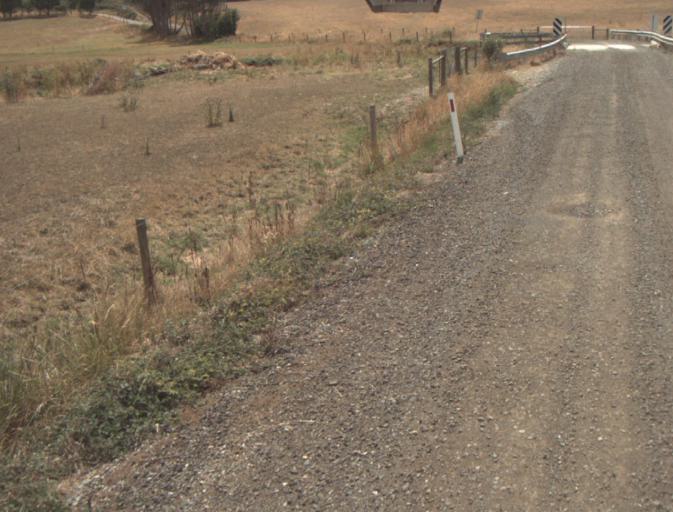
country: AU
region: Tasmania
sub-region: Launceston
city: Mayfield
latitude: -41.2128
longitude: 147.1487
